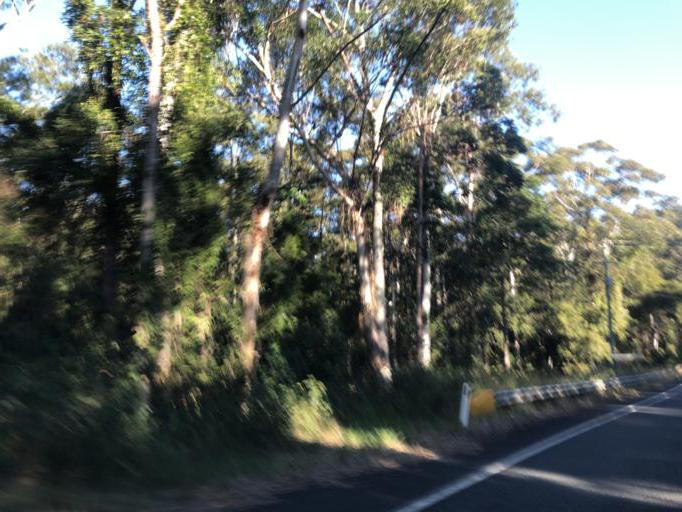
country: AU
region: New South Wales
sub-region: Nambucca Shire
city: Nambucca
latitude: -30.5513
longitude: 153.0085
